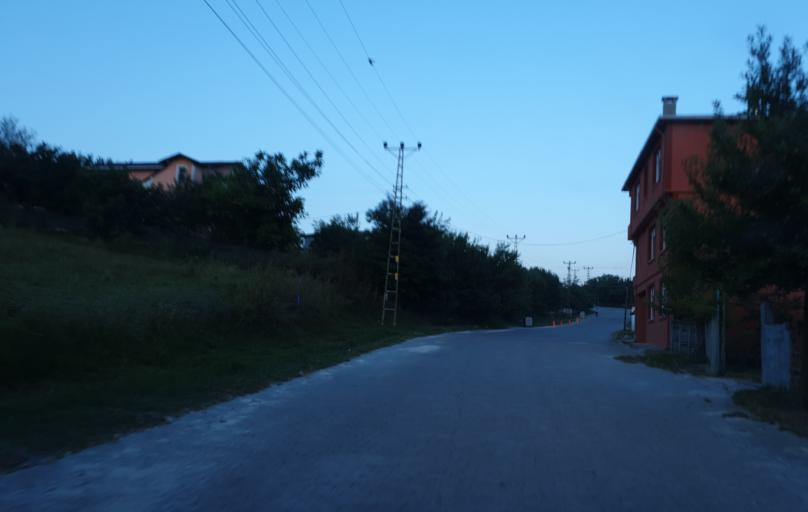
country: TR
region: Tekirdag
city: Velimese
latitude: 41.3503
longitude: 27.8800
